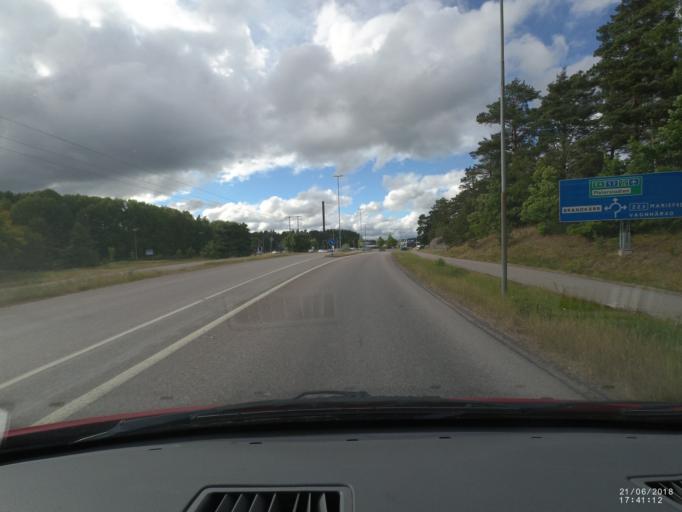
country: SE
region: Soedermanland
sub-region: Nykopings Kommun
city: Nykoping
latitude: 58.7658
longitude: 17.0275
